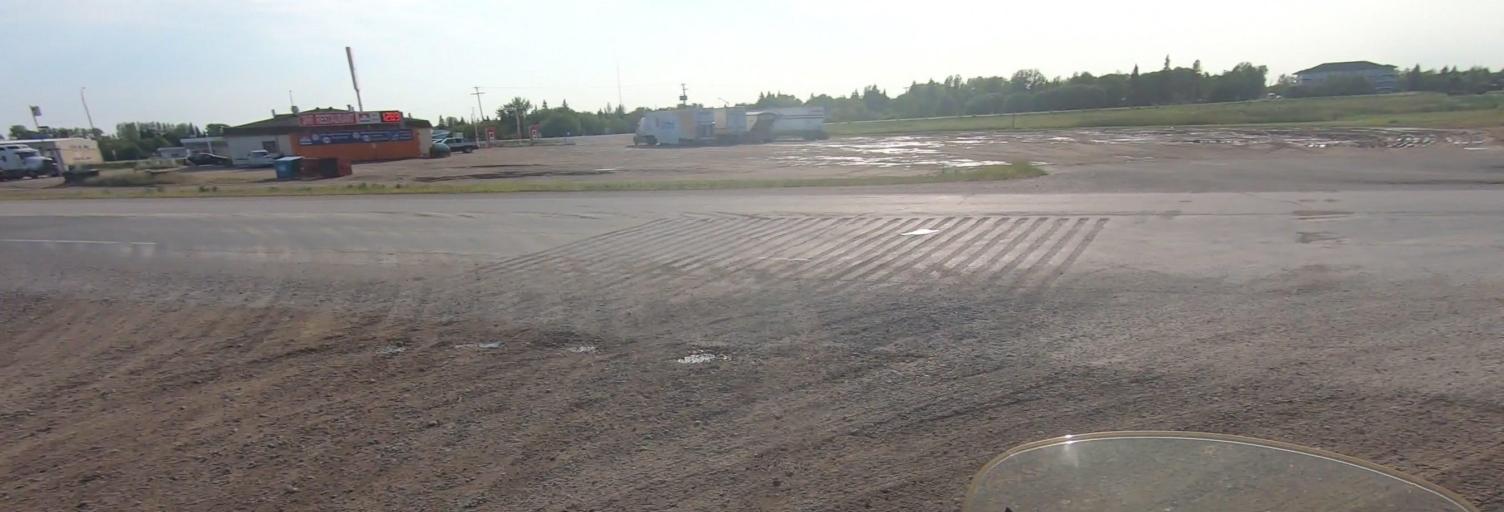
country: CA
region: Saskatchewan
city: Esterhazy
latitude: 50.3342
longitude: -102.2581
